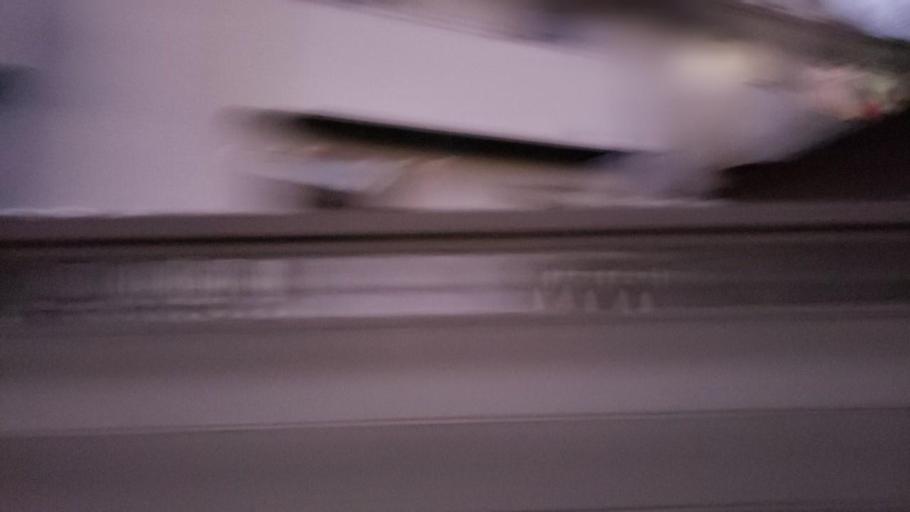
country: JP
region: Tokushima
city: Kamojimacho-jogejima
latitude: 34.0883
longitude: 134.2904
